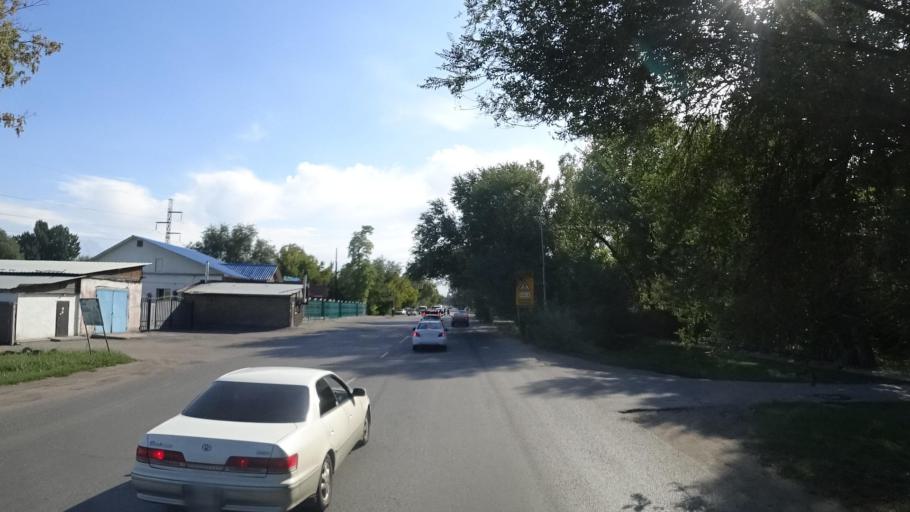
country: KZ
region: Almaty Oblysy
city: Energeticheskiy
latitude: 43.3856
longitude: 77.0004
